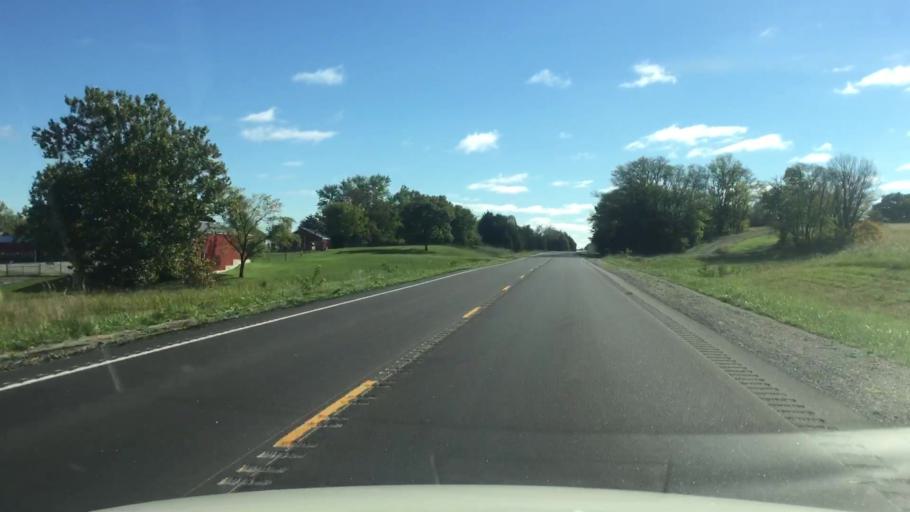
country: US
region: Missouri
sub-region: Boone County
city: Columbia
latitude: 38.9897
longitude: -92.5118
